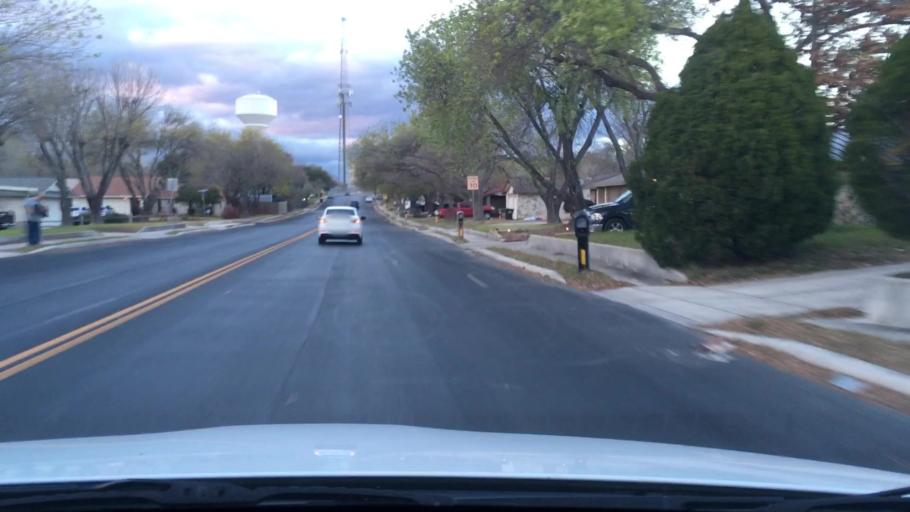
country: US
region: Texas
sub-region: Bexar County
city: Windcrest
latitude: 29.5260
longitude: -98.3530
